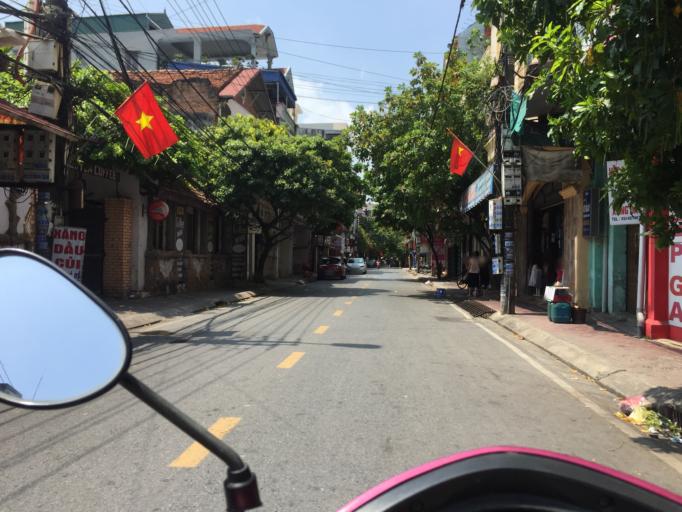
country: VN
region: Nam Dinh
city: Thanh Pho Nam Dinh
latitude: 20.4271
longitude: 106.1769
